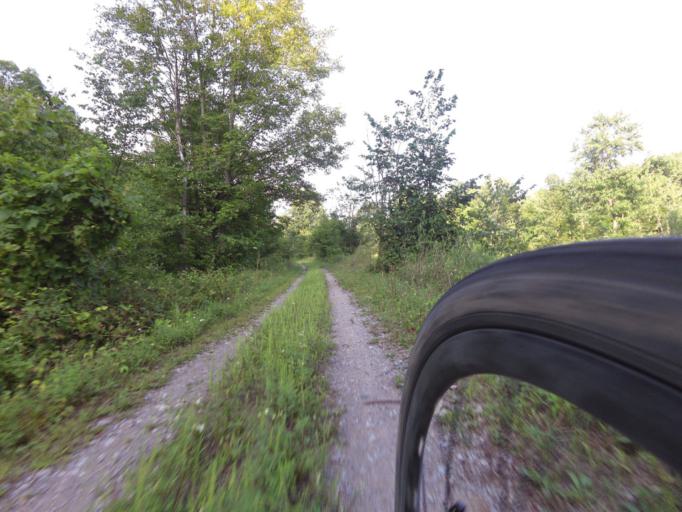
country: CA
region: Ontario
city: Kingston
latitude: 44.5082
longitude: -76.4272
